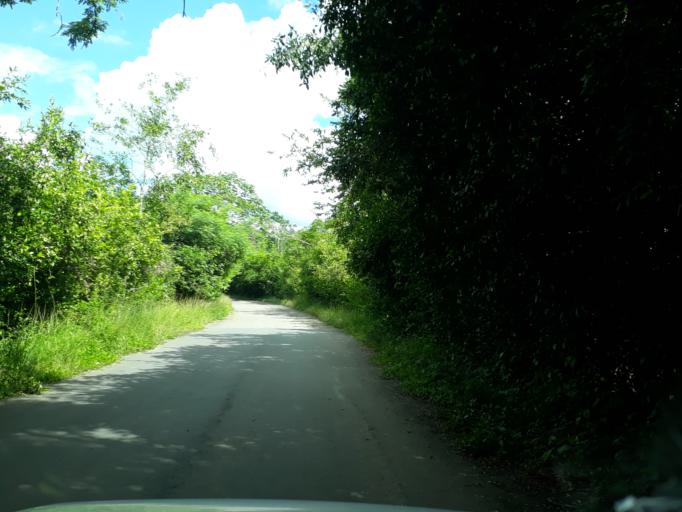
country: CO
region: Cundinamarca
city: Medina
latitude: 4.5214
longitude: -73.3563
